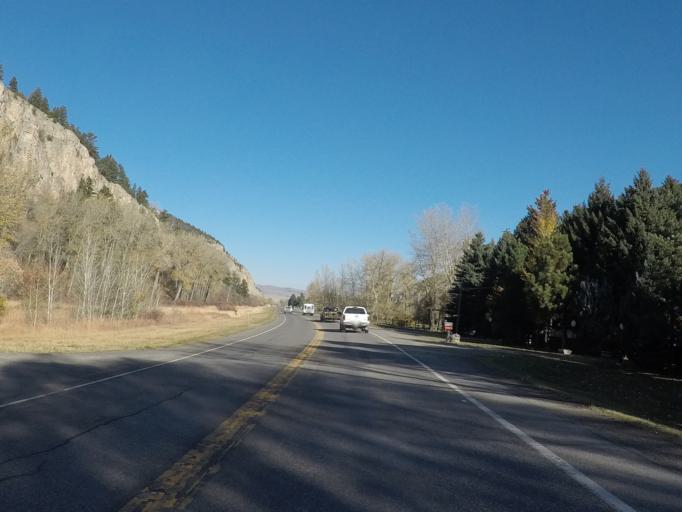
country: US
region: Montana
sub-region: Park County
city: Livingston
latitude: 45.5950
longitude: -110.5711
